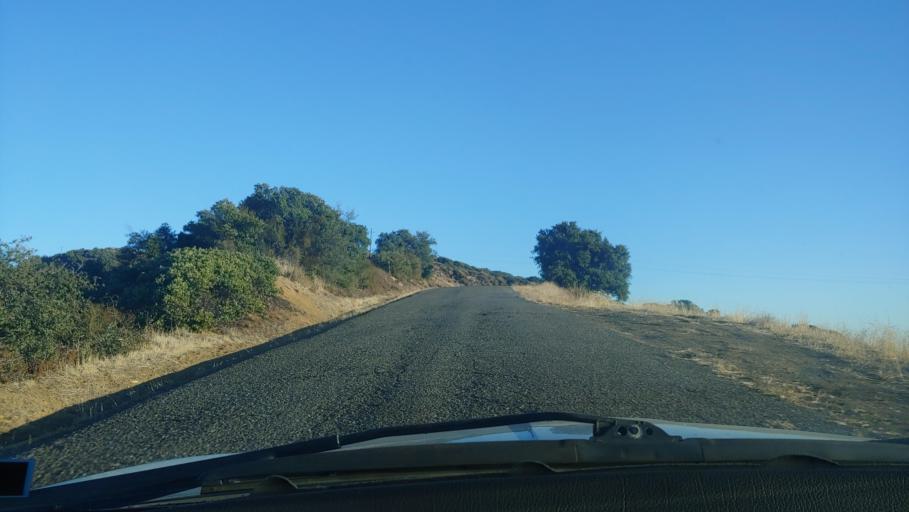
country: US
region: California
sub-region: Santa Barbara County
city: Mission Canyon
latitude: 34.5151
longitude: -119.7783
